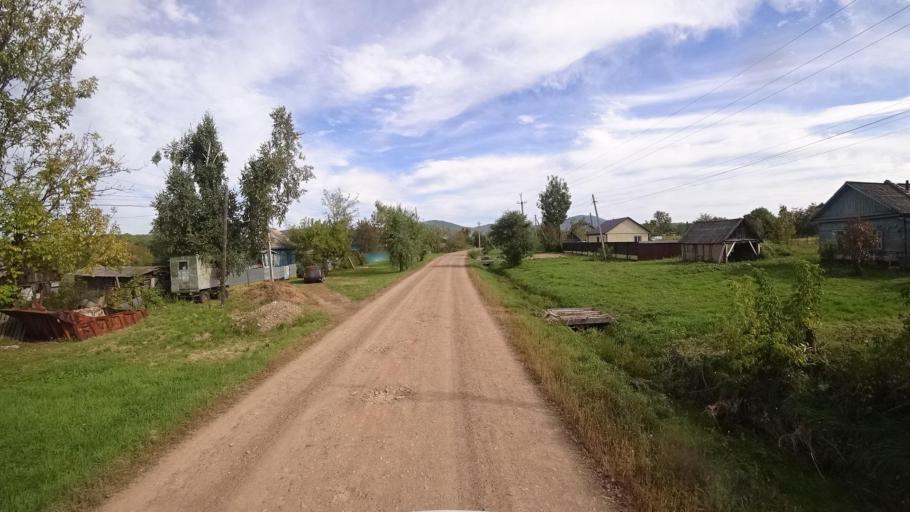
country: RU
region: Primorskiy
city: Dostoyevka
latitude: 44.3055
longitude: 133.4595
